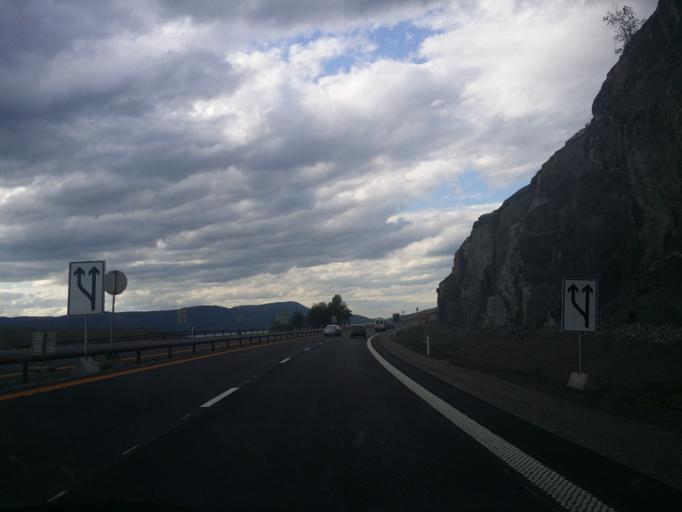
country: NO
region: Akershus
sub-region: Eidsvoll
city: Eidsvoll
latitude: 60.4525
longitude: 11.2404
